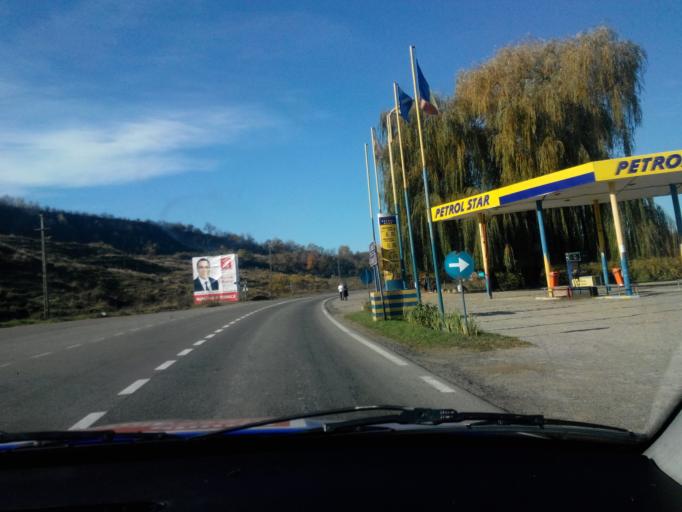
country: RO
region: Bacau
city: Caiuti-Sat
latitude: 46.1834
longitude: 26.9365
